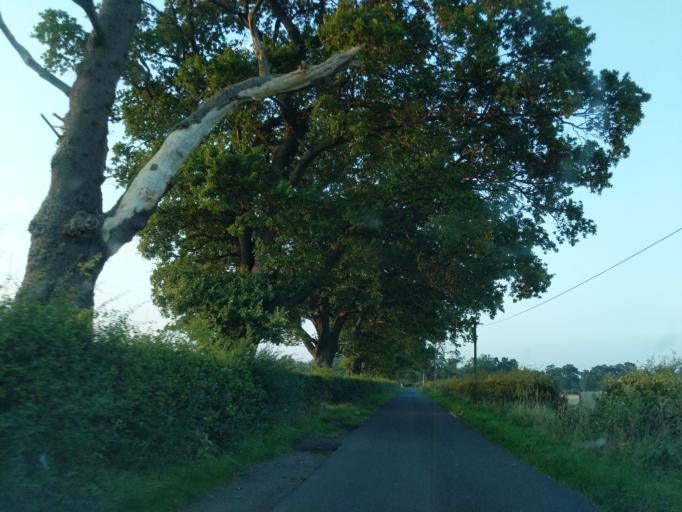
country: GB
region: Scotland
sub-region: Stirling
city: Doune
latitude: 56.1263
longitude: -4.0579
